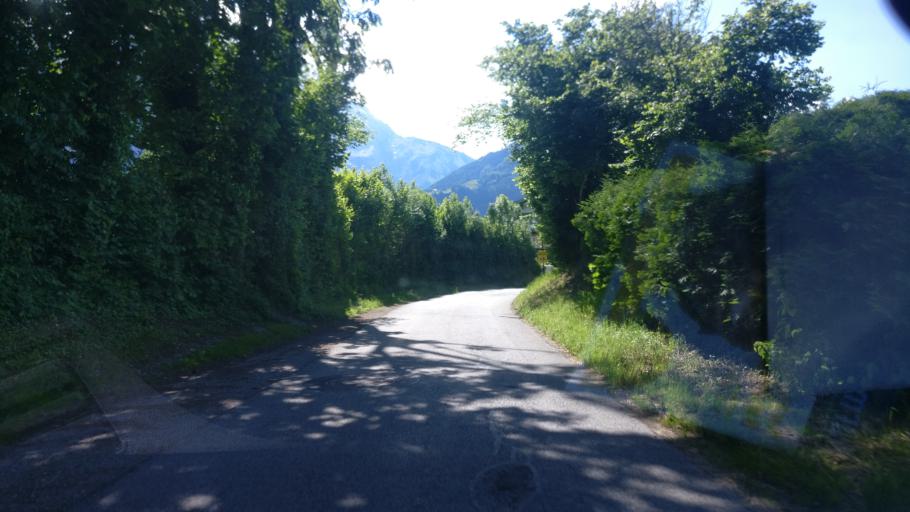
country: AT
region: Salzburg
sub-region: Politischer Bezirk Hallein
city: Golling an der Salzach
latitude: 47.6177
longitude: 13.1685
